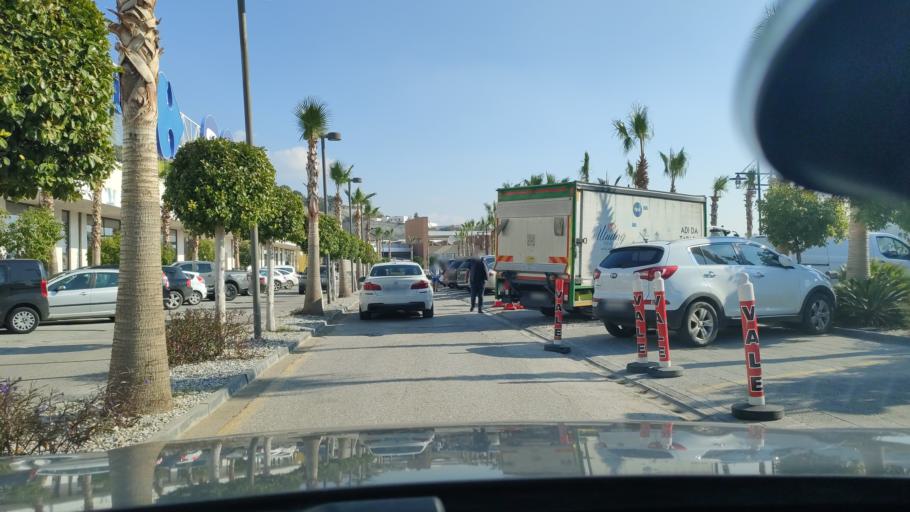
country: TR
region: Mugla
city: Ortakent
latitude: 37.0581
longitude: 27.3564
